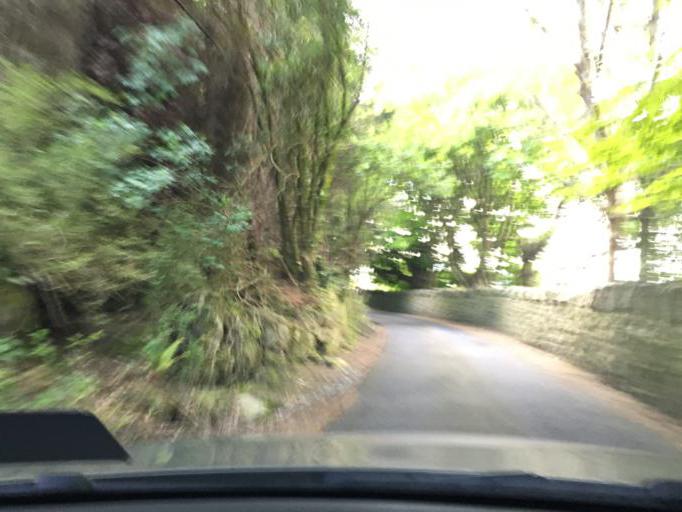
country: IE
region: Leinster
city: Ballinteer
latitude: 53.2556
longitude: -6.2786
